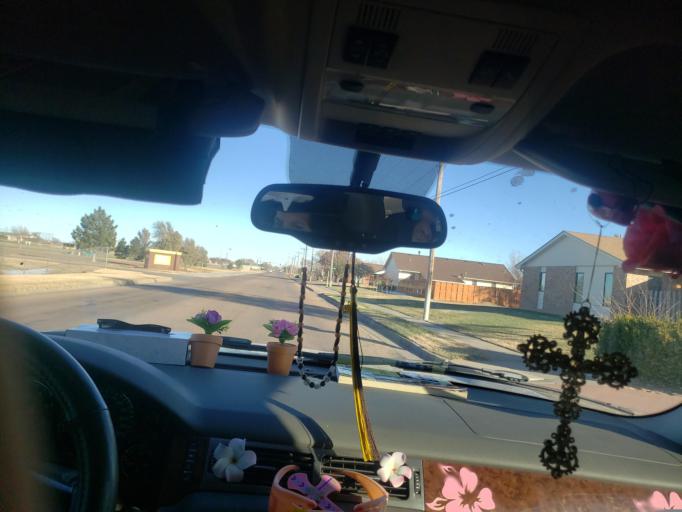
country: US
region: Kansas
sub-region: Finney County
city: Garden City
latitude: 37.9674
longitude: -100.8449
